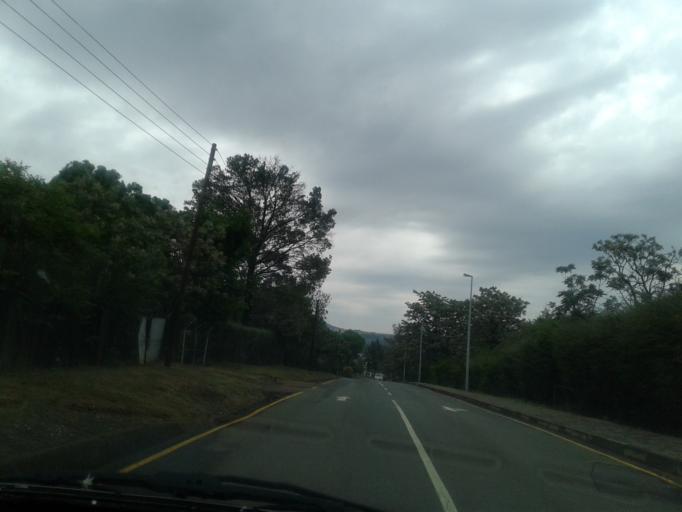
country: LS
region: Maseru
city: Maseru
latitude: -29.3045
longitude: 27.4710
